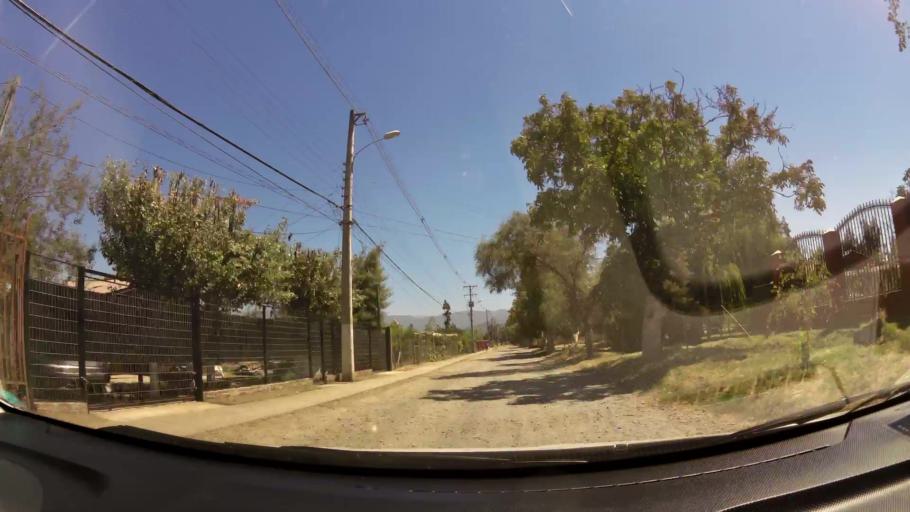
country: CL
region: O'Higgins
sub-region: Provincia de Cachapoal
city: Rancagua
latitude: -34.1523
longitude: -70.7504
